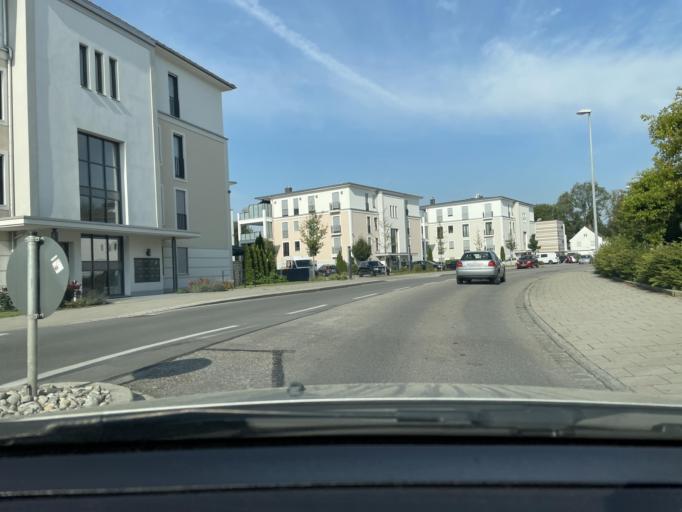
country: DE
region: Bavaria
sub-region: Upper Bavaria
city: Muehldorf
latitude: 48.2443
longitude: 12.5157
